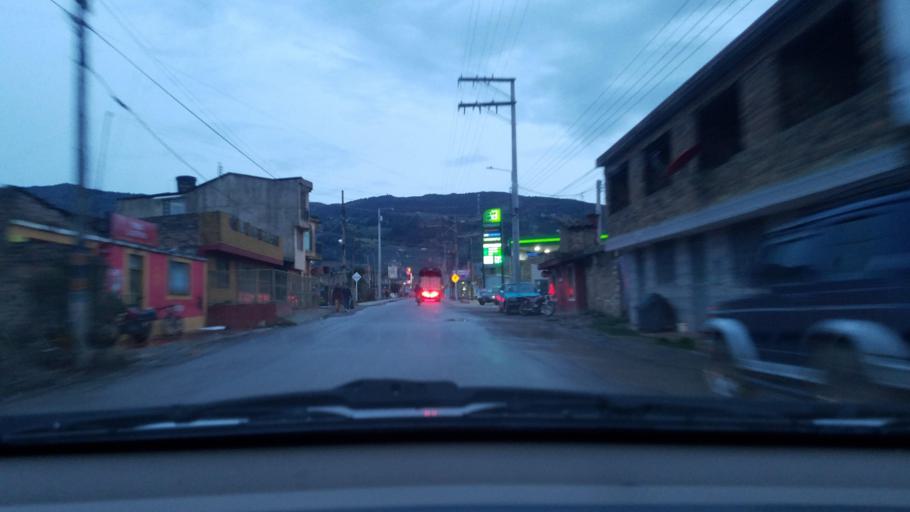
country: CO
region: Boyaca
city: Aquitania
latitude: 5.5246
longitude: -72.8833
